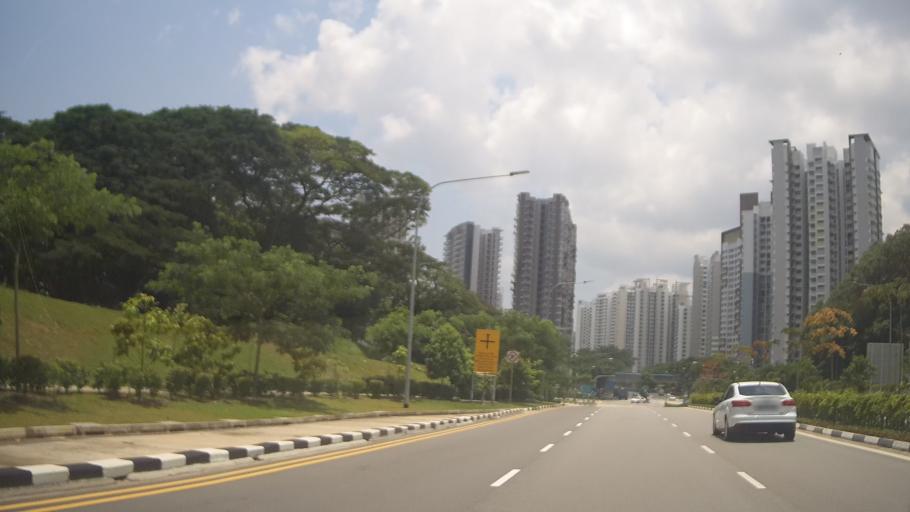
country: MY
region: Johor
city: Kampung Pasir Gudang Baru
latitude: 1.3952
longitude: 103.8713
